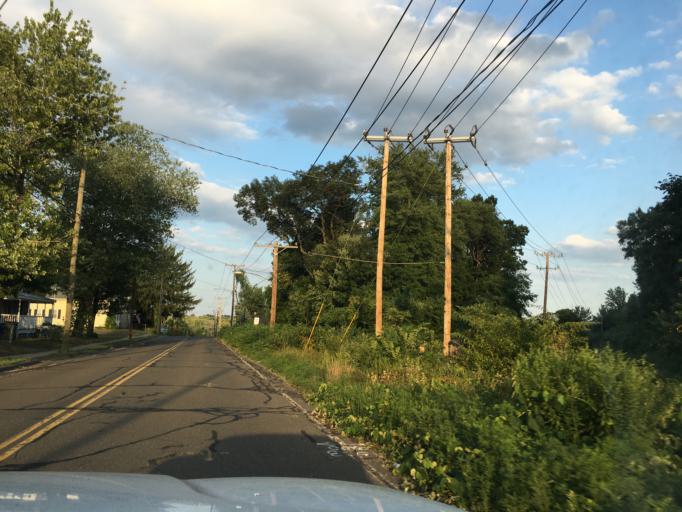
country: US
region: Connecticut
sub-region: Hartford County
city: Windsor Locks
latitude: 41.9195
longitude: -72.6288
